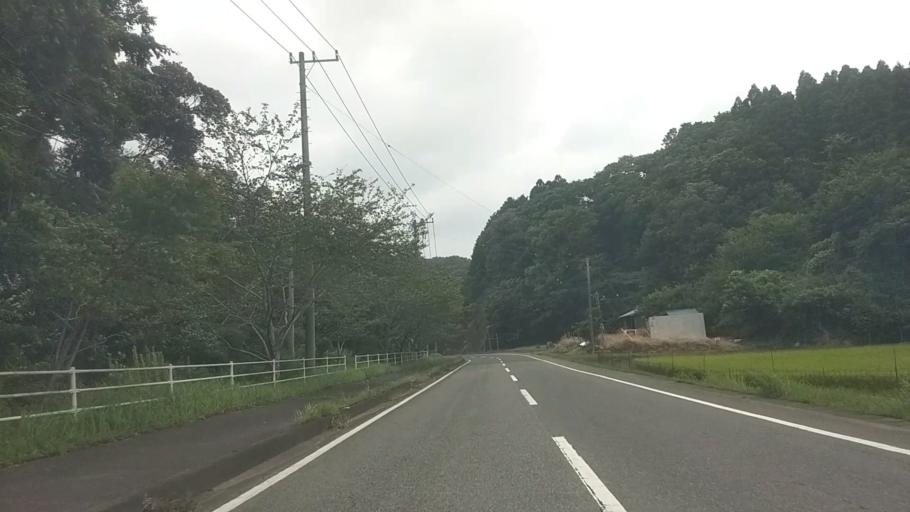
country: JP
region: Chiba
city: Kawaguchi
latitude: 35.2477
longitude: 140.0385
